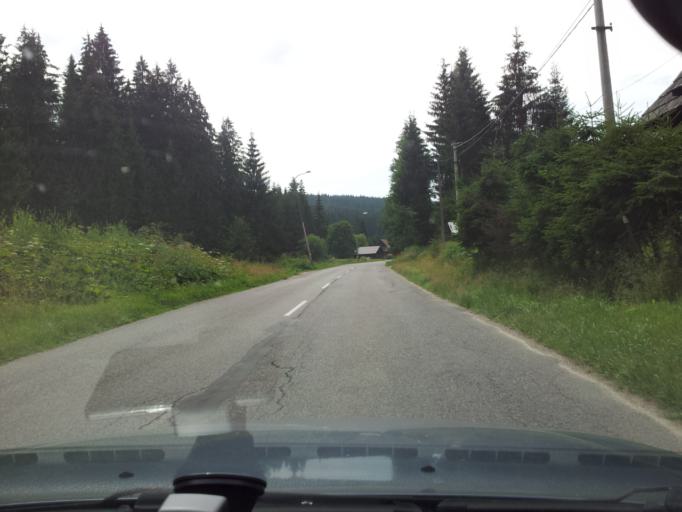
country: SK
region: Zilinsky
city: Oravska Lesna
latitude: 49.3719
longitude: 19.2174
